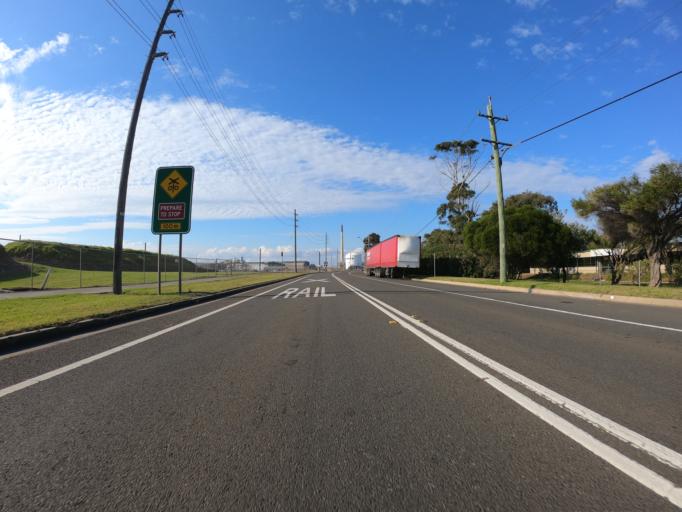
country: AU
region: New South Wales
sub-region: Wollongong
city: Port Kembla
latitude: -34.4745
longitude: 150.9017
